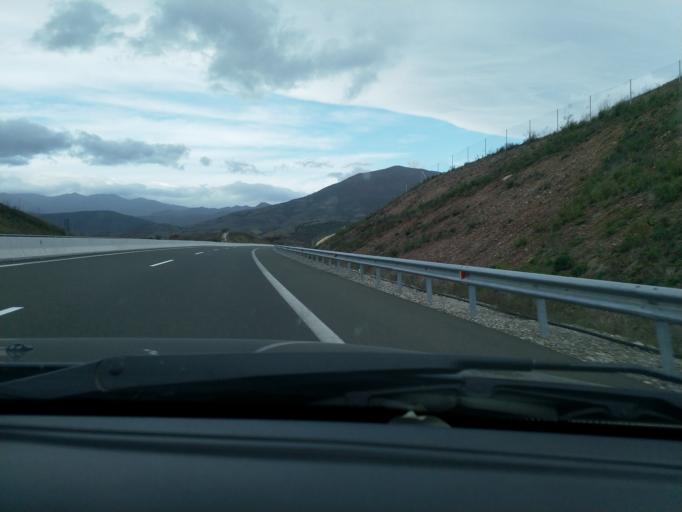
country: GR
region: Thessaly
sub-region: Nomos Kardhitsas
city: Anavra
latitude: 39.1537
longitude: 22.1173
